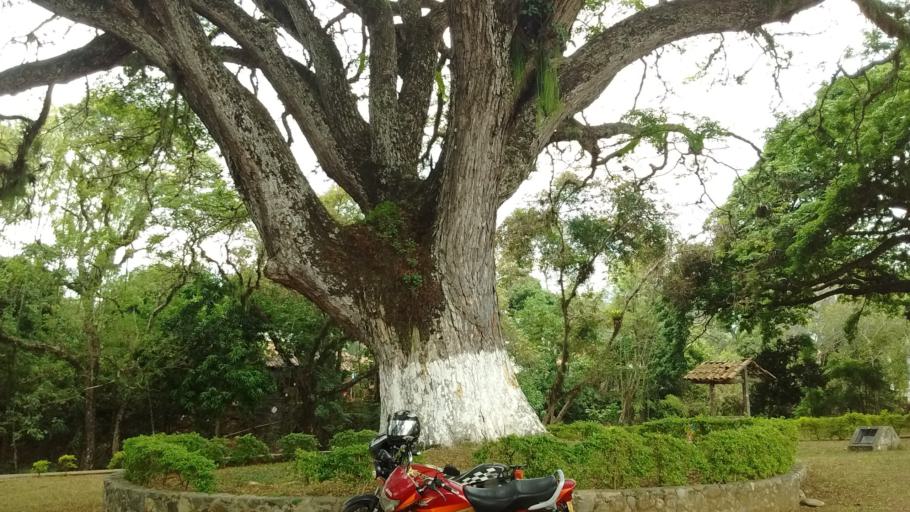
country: CO
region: Cauca
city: Caloto
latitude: 3.0341
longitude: -76.4068
